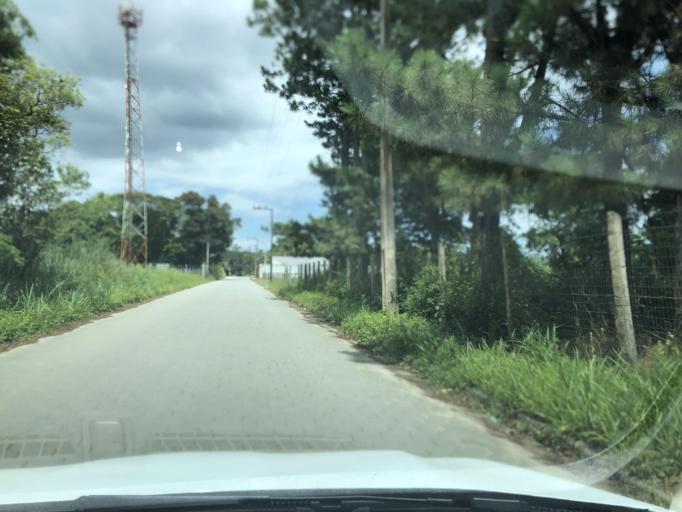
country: BR
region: Santa Catarina
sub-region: Sao Francisco Do Sul
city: Sao Francisco do Sul
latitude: -26.2268
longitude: -48.5821
